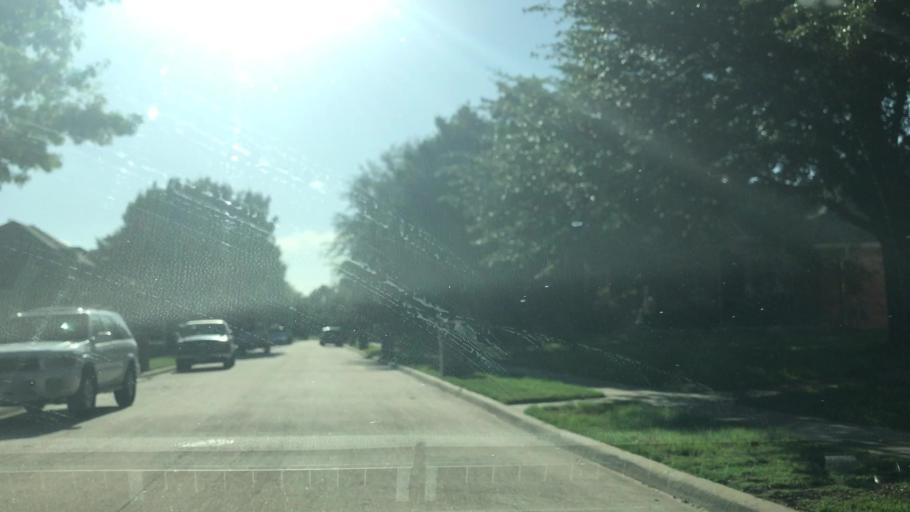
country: US
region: Texas
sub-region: Collin County
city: Frisco
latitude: 33.1224
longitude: -96.7798
